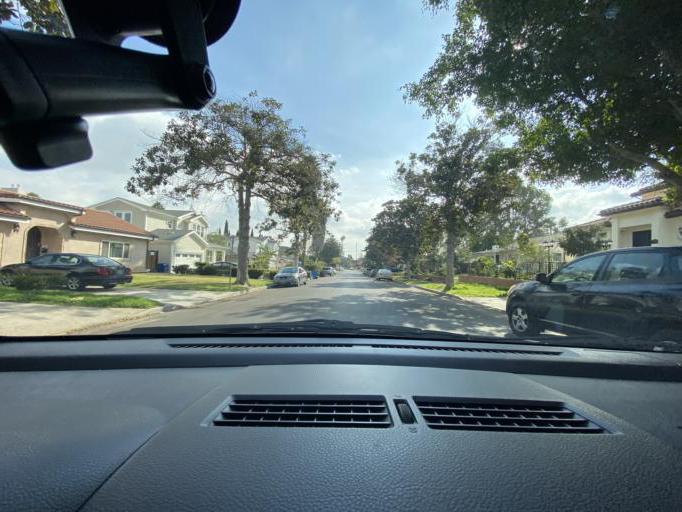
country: US
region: California
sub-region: Los Angeles County
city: Culver City
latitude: 34.0207
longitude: -118.4168
